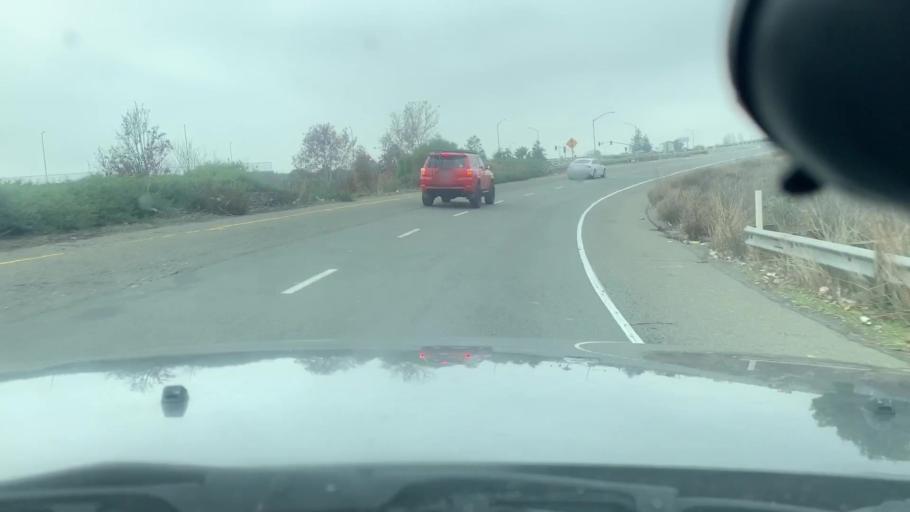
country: US
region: California
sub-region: Alameda County
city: Fremont
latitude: 37.5292
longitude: -122.0002
